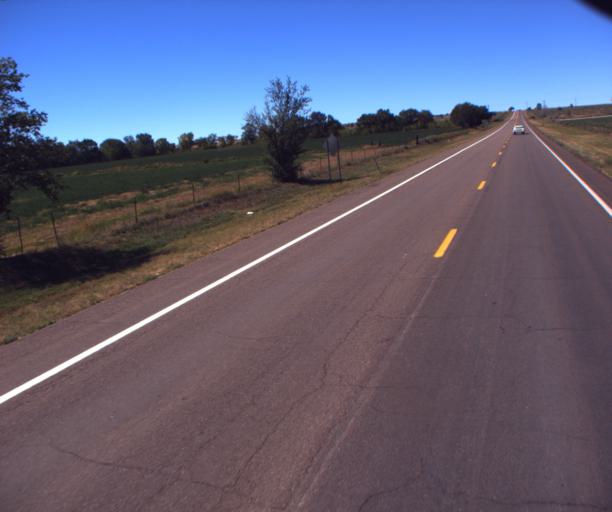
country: US
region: Arizona
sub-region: Apache County
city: Saint Johns
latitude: 34.5063
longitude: -109.3975
